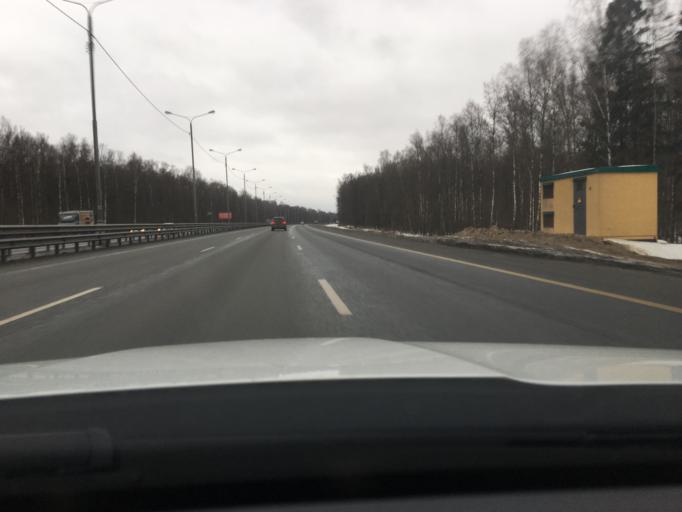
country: RU
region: Moskovskaya
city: Novyy Byt
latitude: 55.1055
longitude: 37.5832
